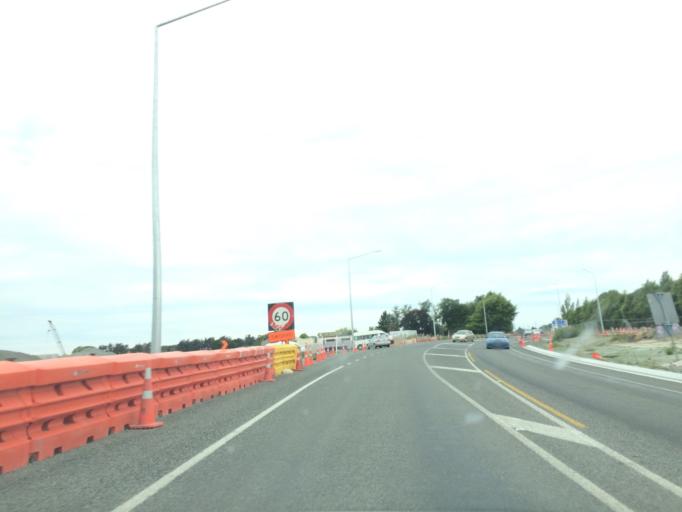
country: NZ
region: Canterbury
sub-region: Waimakariri District
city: Kaiapoi
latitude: -43.4528
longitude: 172.6067
